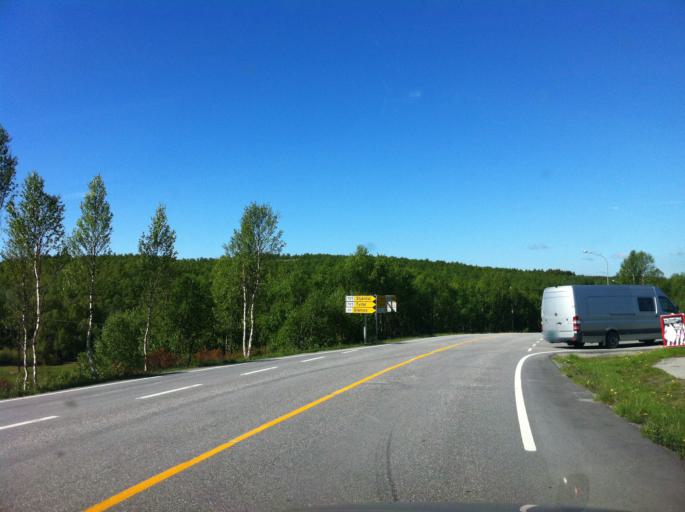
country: NO
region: Sor-Trondelag
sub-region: Tydal
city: Aas
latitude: 62.6460
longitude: 11.8658
